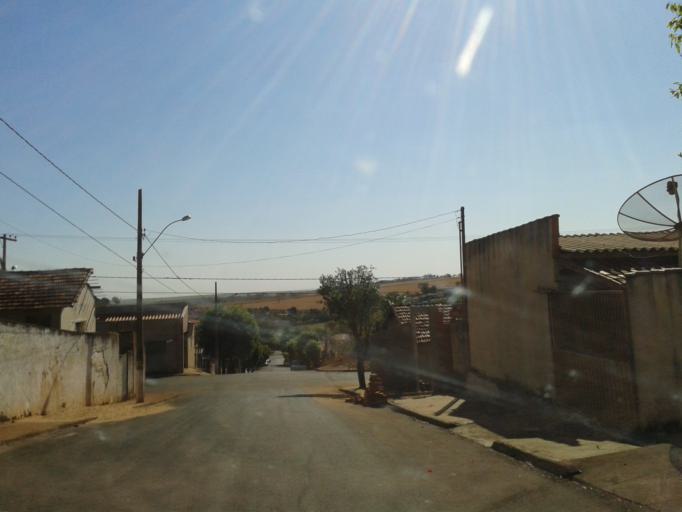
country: BR
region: Minas Gerais
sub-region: Capinopolis
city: Capinopolis
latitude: -18.6804
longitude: -49.5688
